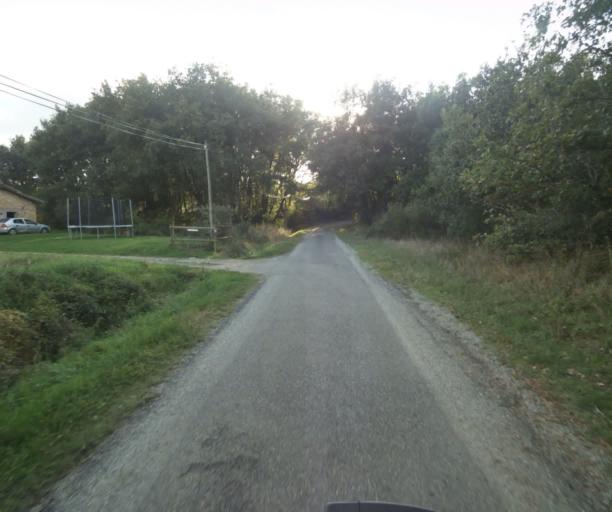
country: FR
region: Midi-Pyrenees
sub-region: Departement de la Haute-Garonne
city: Launac
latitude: 43.8161
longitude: 1.1339
